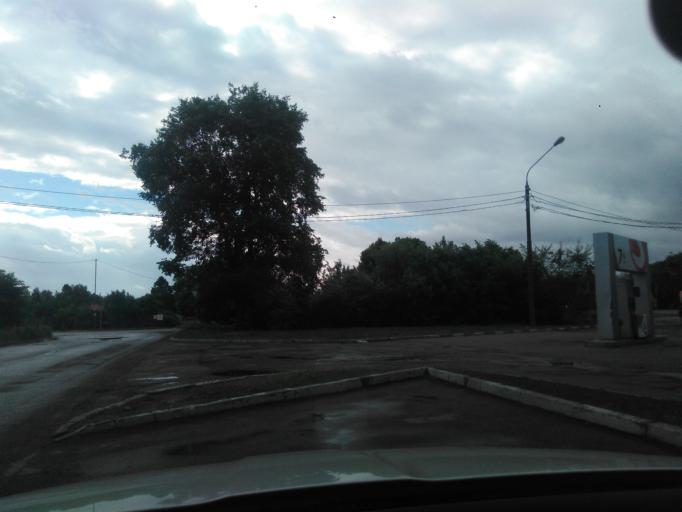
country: RU
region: Moskovskaya
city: Novopodrezkovo
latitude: 55.9395
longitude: 37.3680
